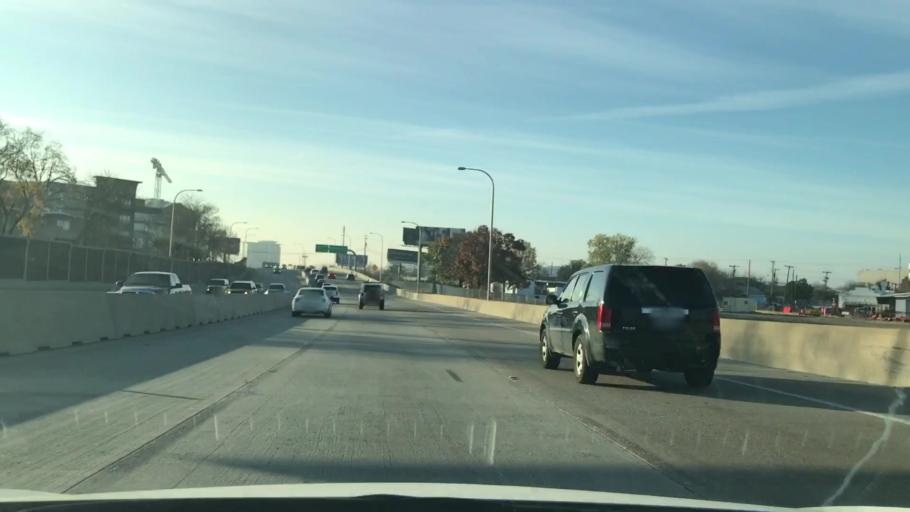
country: US
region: Texas
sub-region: Dallas County
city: Dallas
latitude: 32.8107
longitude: -96.8182
